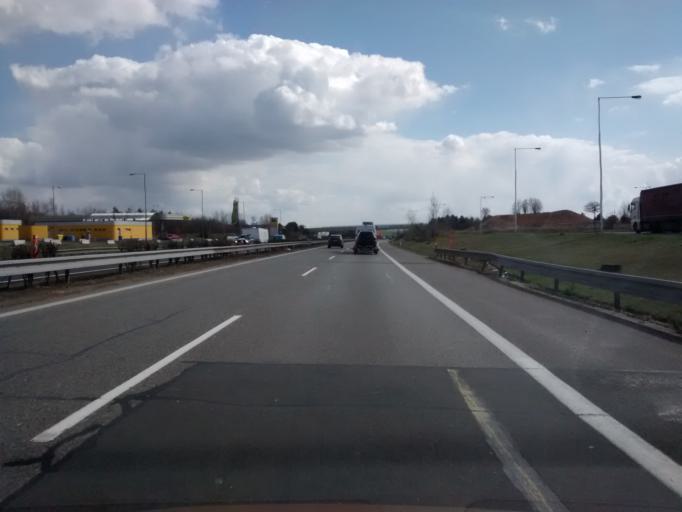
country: CZ
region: Central Bohemia
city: Odolena Voda
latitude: 50.2077
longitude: 14.4343
